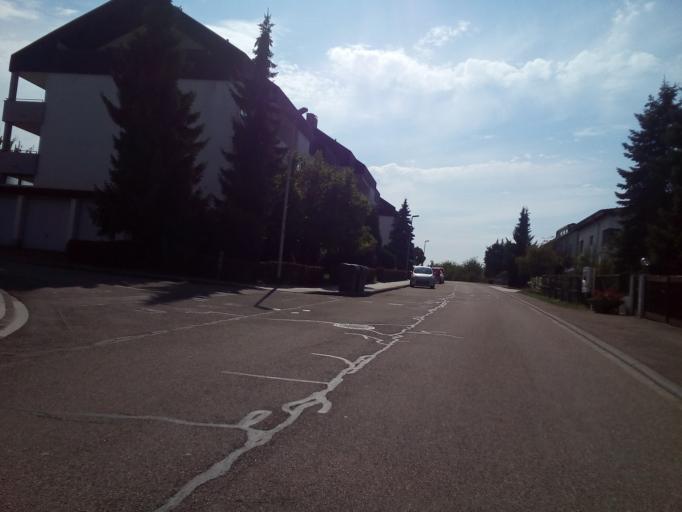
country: DE
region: Baden-Wuerttemberg
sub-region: Freiburg Region
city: Lauf
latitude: 48.6527
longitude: 8.1272
